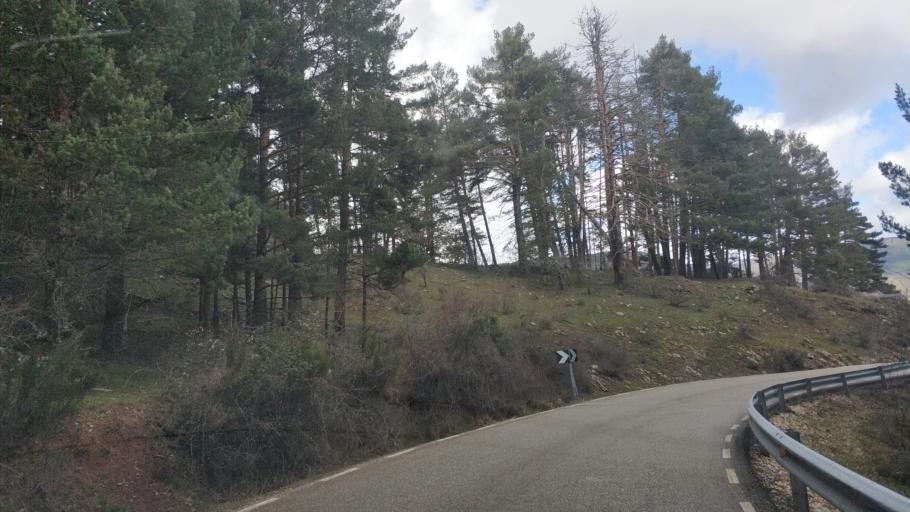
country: ES
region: Castille and Leon
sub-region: Provincia de Burgos
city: Neila
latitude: 42.0532
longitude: -3.0114
